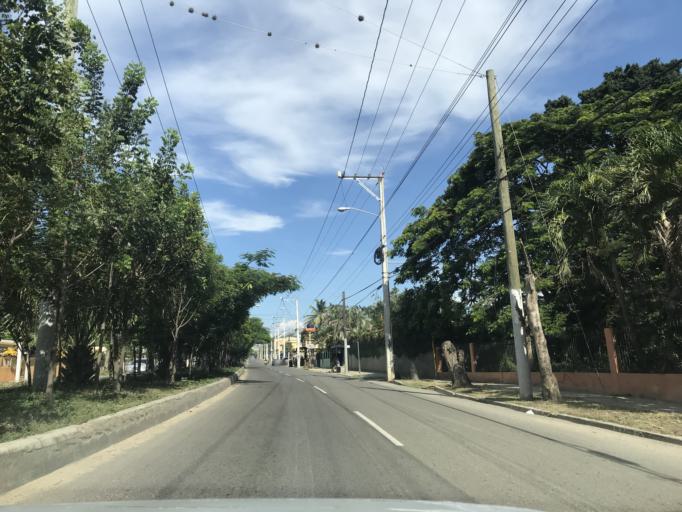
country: DO
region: Santiago
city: Santiago de los Caballeros
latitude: 19.4444
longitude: -70.7401
